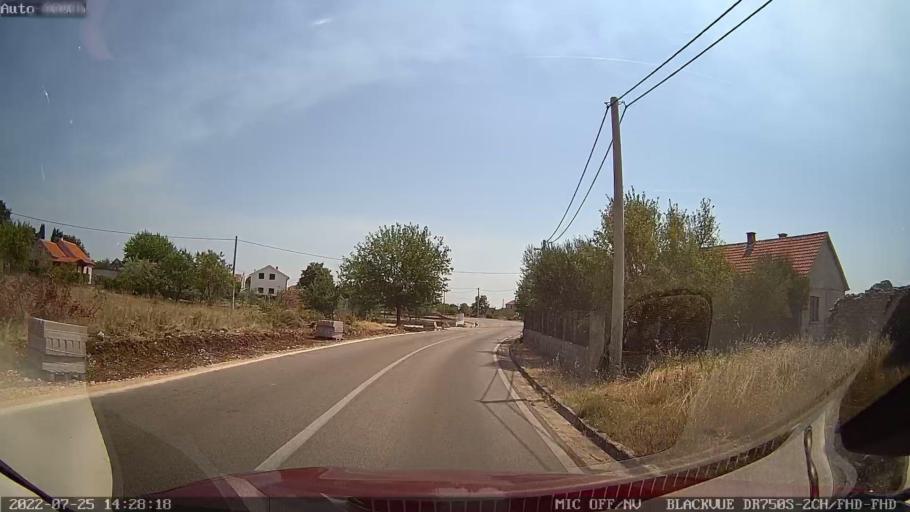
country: HR
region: Zadarska
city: Policnik
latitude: 44.1270
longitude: 15.3483
